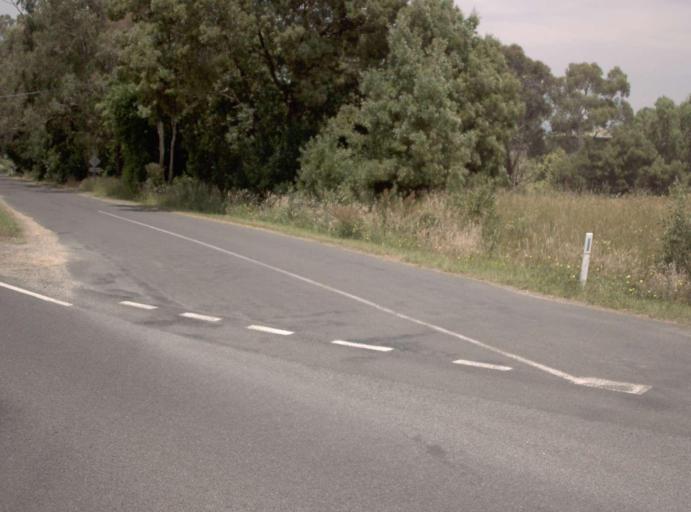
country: AU
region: Victoria
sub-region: Latrobe
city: Traralgon
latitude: -38.2951
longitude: 146.7019
